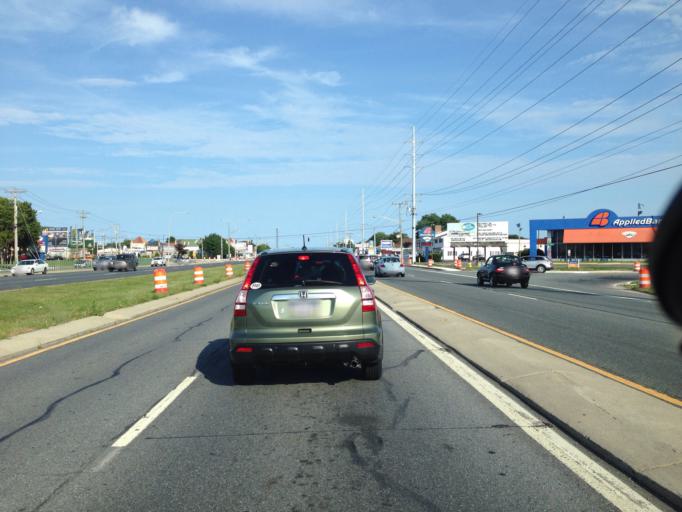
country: US
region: Delaware
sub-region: Sussex County
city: Rehoboth Beach
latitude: 38.7133
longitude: -75.1039
